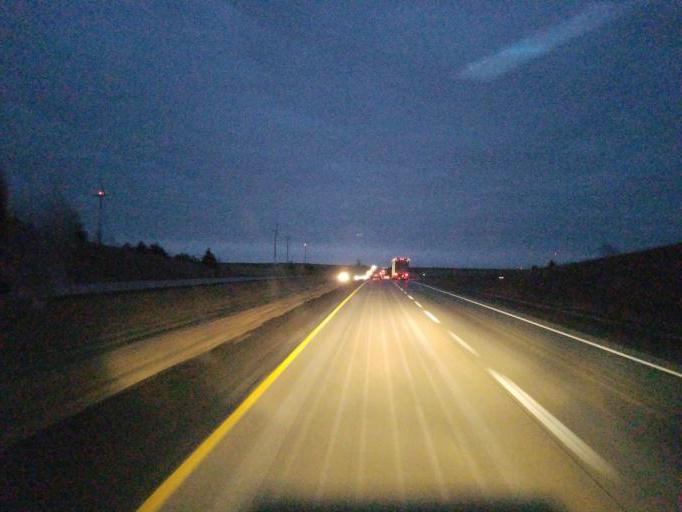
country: US
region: Iowa
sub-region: Guthrie County
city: Guthrie Center
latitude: 41.4969
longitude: -94.7109
